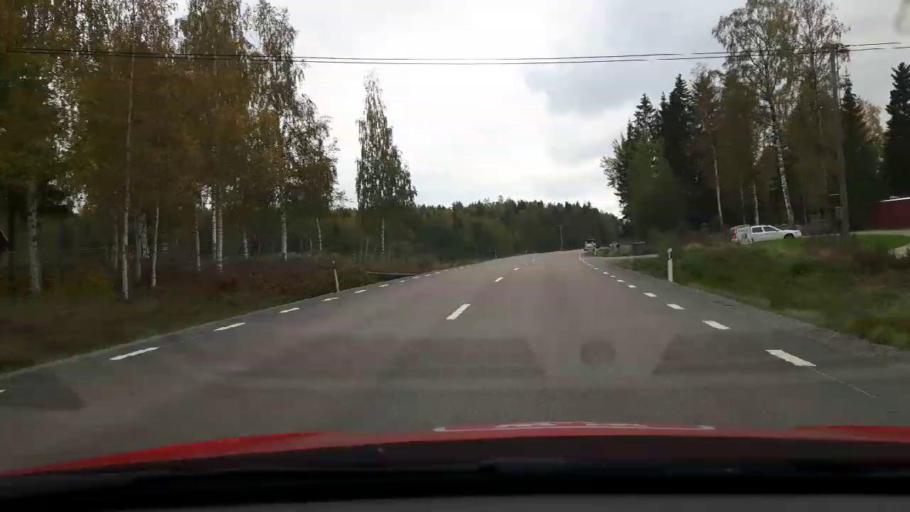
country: SE
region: Gaevleborg
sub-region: Bollnas Kommun
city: Bollnas
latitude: 61.3081
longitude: 16.4586
